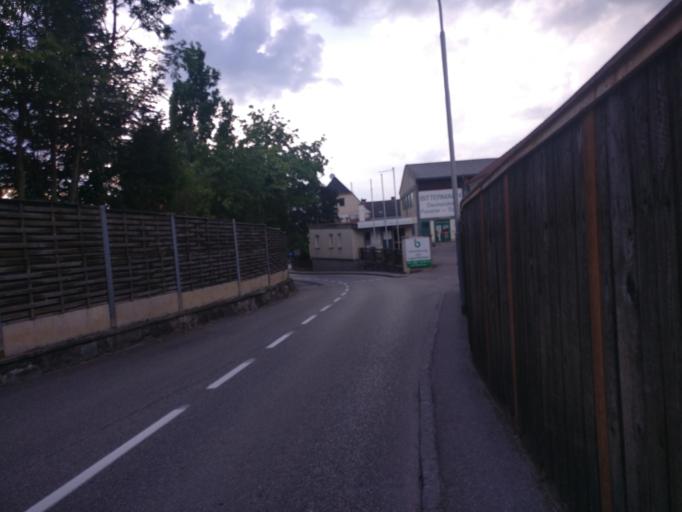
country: AT
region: Upper Austria
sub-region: Politischer Bezirk Steyr-Land
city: Sankt Ulrich bei Steyr
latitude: 48.0303
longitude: 14.4198
